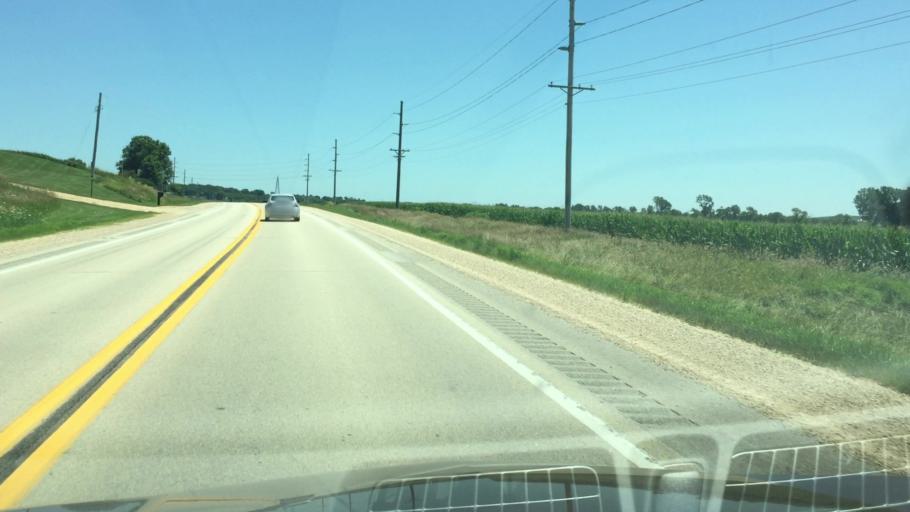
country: US
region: Iowa
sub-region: Jackson County
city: Maquoketa
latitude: 42.0670
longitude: -90.7804
